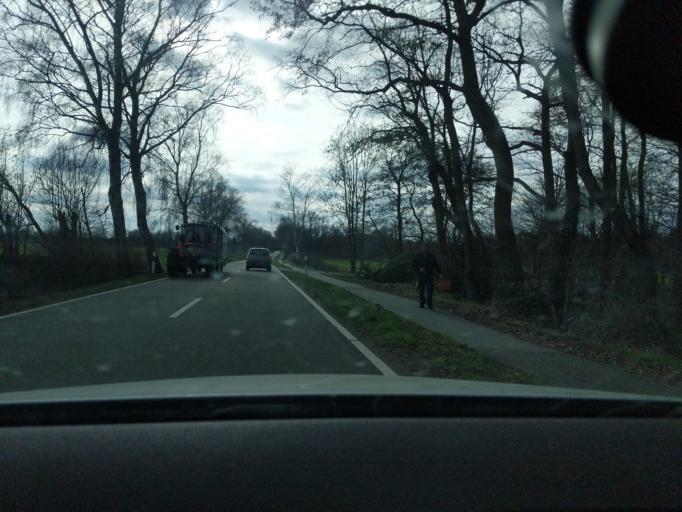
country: DE
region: Lower Saxony
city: Engelschoff
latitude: 53.6385
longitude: 9.3286
